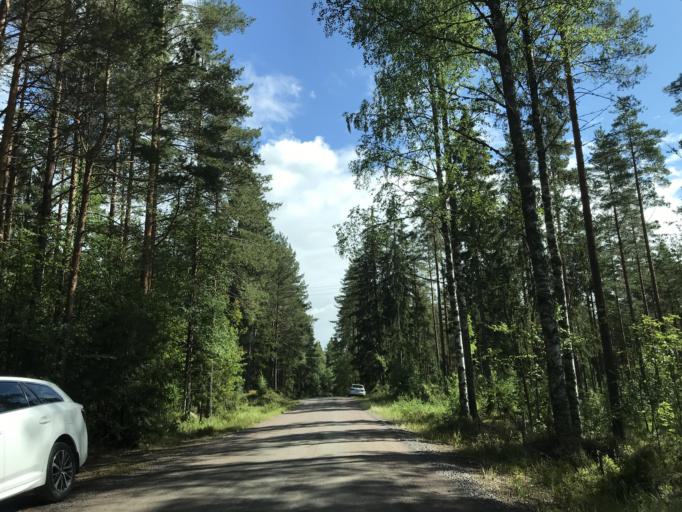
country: FI
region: Uusimaa
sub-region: Helsinki
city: Kaerkoelae
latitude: 60.6256
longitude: 23.7690
